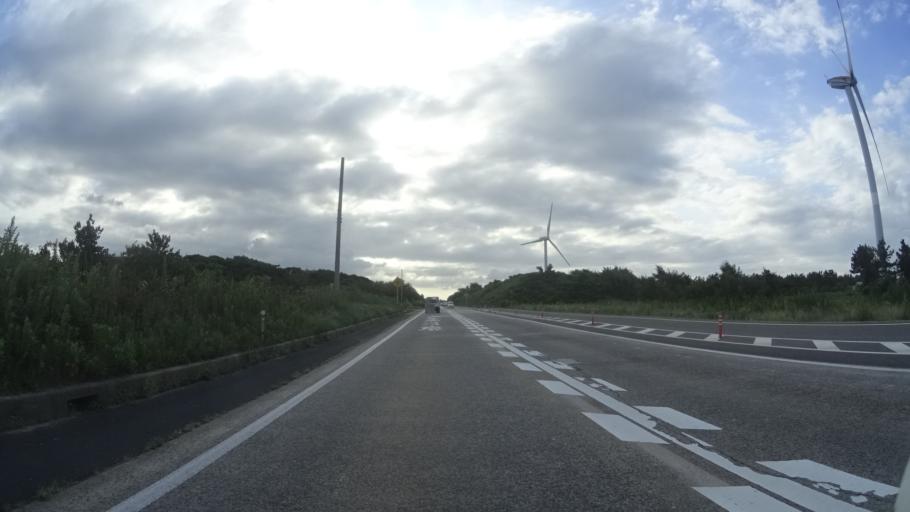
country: JP
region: Tottori
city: Kurayoshi
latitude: 35.4984
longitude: 133.7973
